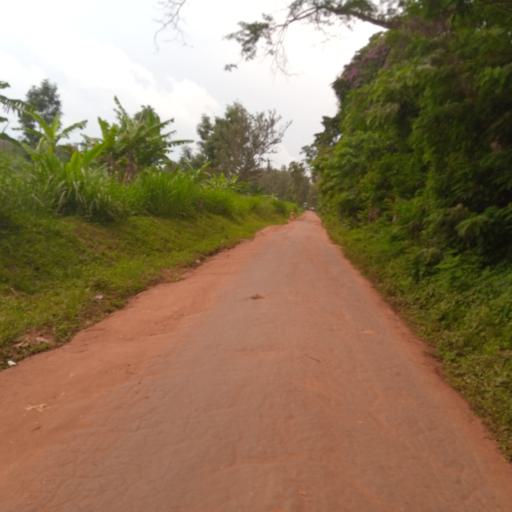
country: UG
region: Eastern Region
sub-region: Mbale District
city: Mbale
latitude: 1.0905
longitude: 34.1858
